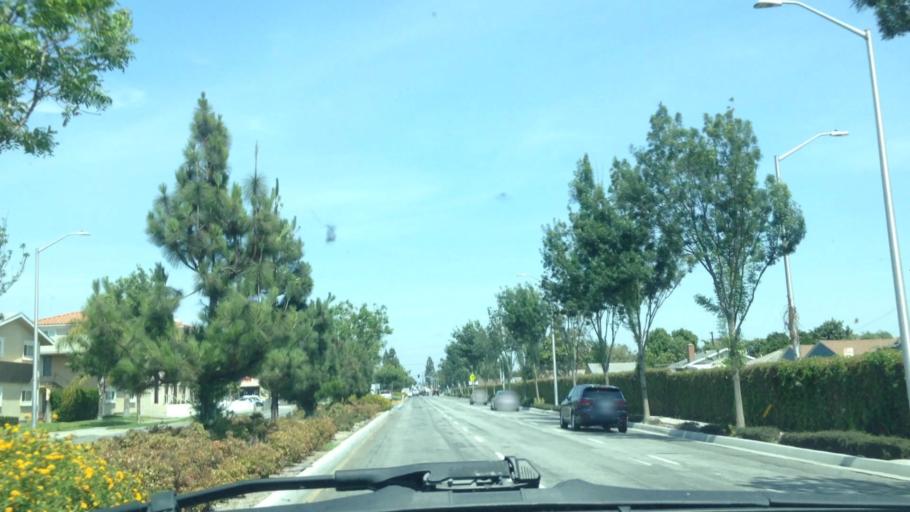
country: US
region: California
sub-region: Los Angeles County
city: Downey
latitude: 33.9171
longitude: -118.1201
